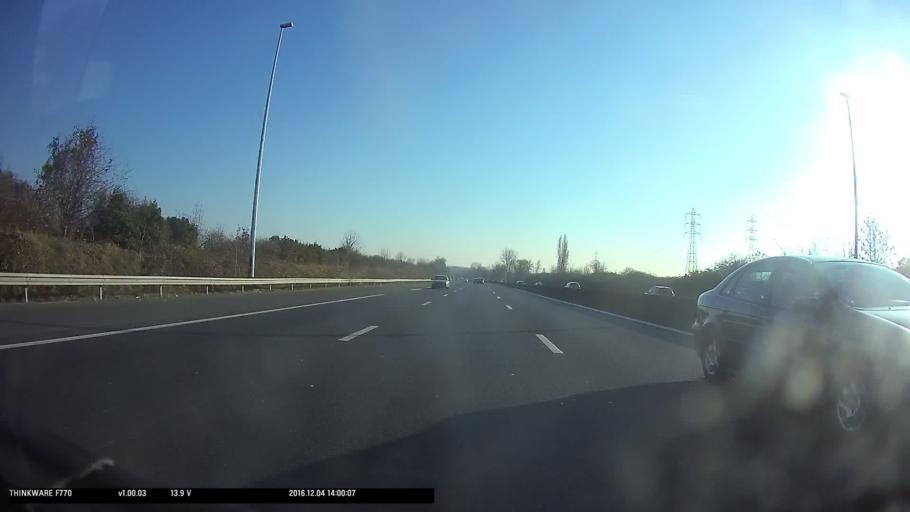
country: FR
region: Ile-de-France
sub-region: Departement du Val-d'Oise
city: Saint-Ouen-l'Aumone
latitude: 49.0255
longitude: 2.1314
